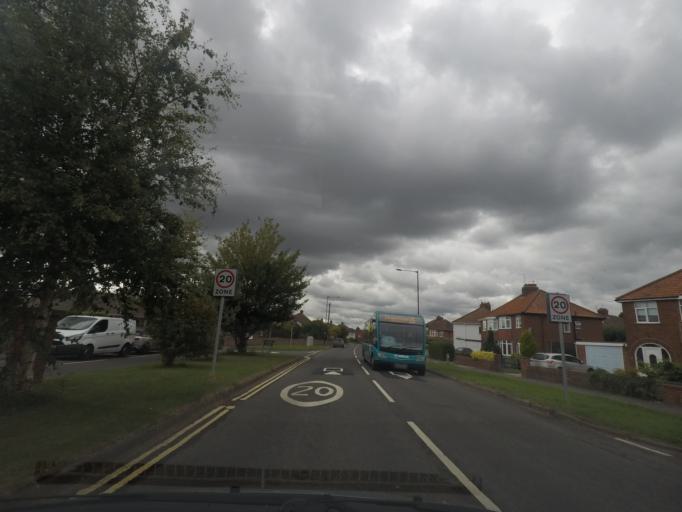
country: GB
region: England
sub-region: City of York
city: Fulford
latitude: 53.9390
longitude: -1.0630
